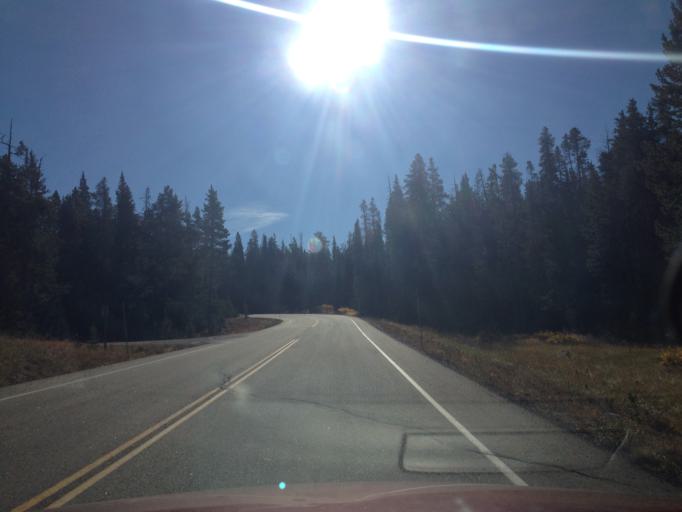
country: US
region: Montana
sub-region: Carbon County
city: Red Lodge
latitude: 45.0272
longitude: -109.8958
